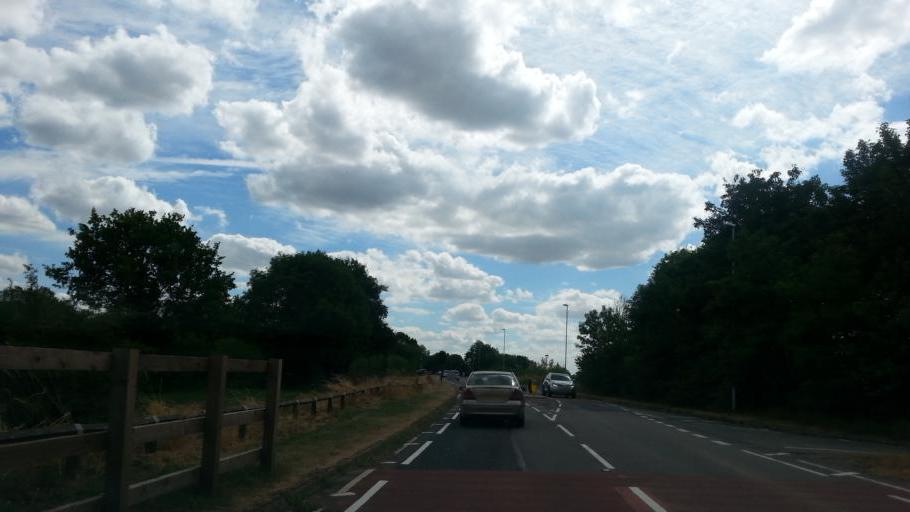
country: GB
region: England
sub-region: Northamptonshire
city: Silverstone
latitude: 52.0977
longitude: -1.0194
